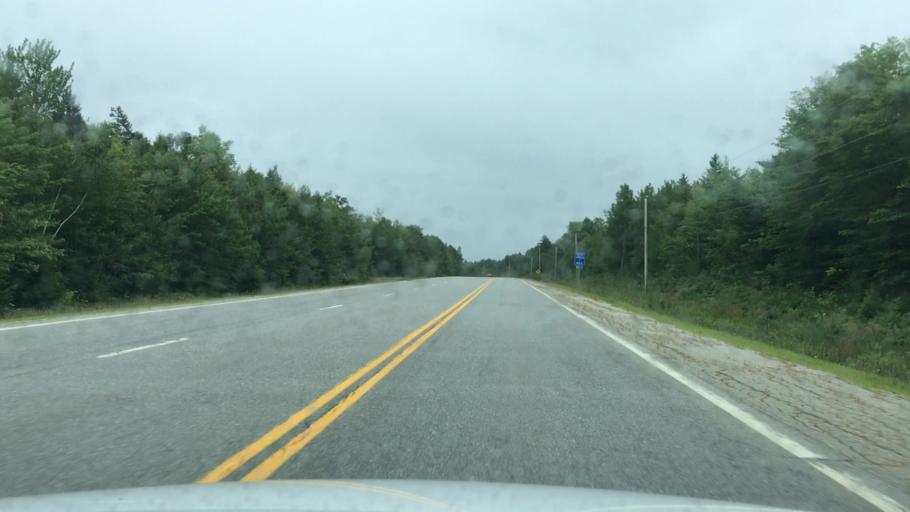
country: US
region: Maine
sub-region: Hancock County
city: Franklin
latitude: 44.8257
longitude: -68.1132
